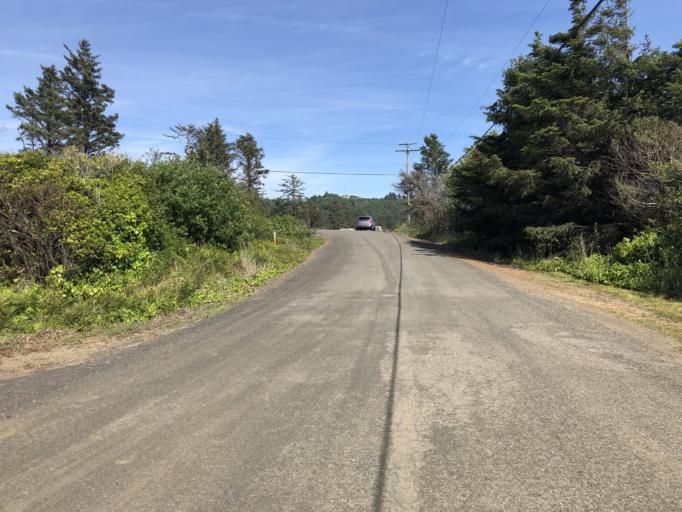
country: US
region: Washington
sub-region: Grays Harbor County
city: Westport
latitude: 46.7368
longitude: -124.0765
